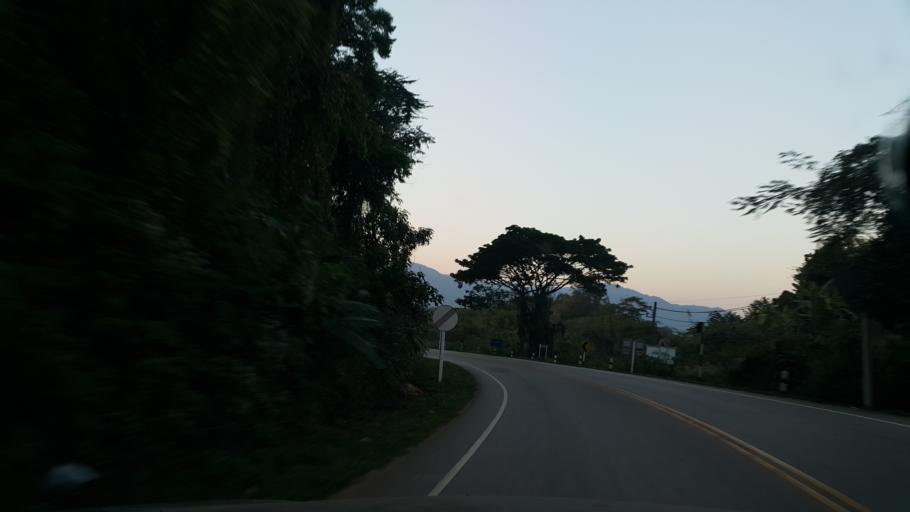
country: TH
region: Phrae
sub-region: Amphoe Wang Chin
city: Wang Chin
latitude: 17.8800
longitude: 99.6198
